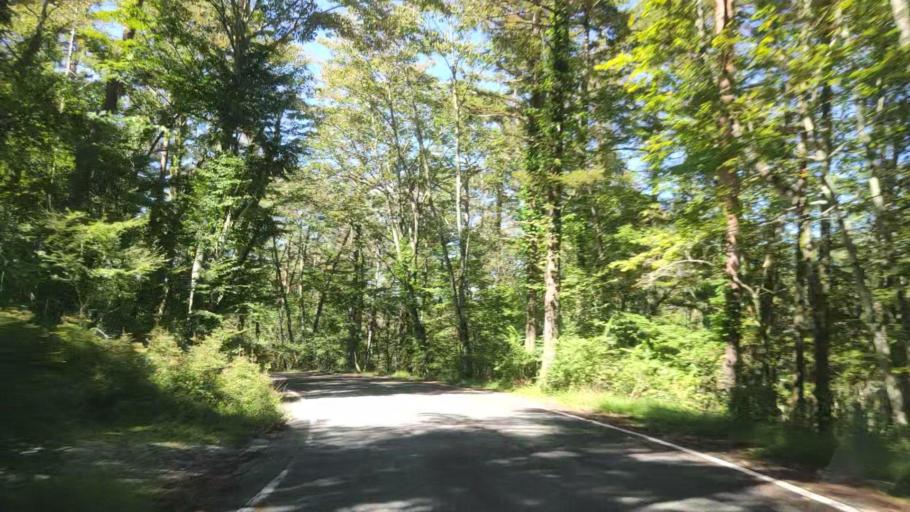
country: JP
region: Shizuoka
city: Gotemba
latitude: 35.4046
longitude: 138.8617
